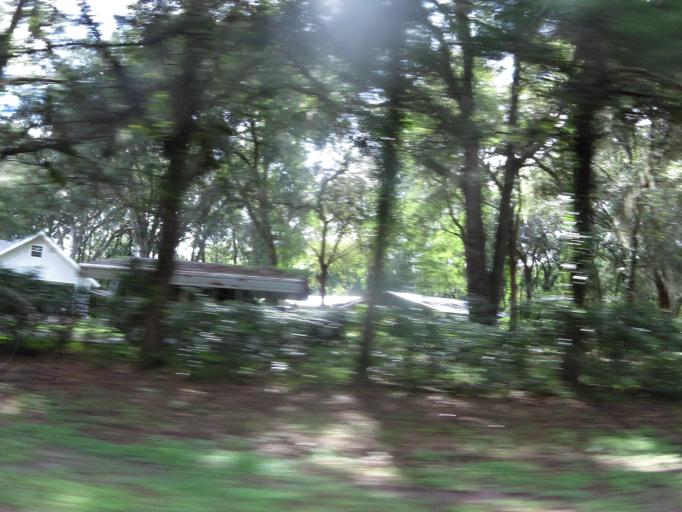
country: US
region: Florida
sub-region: Clay County
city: Green Cove Springs
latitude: 29.9846
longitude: -81.7185
